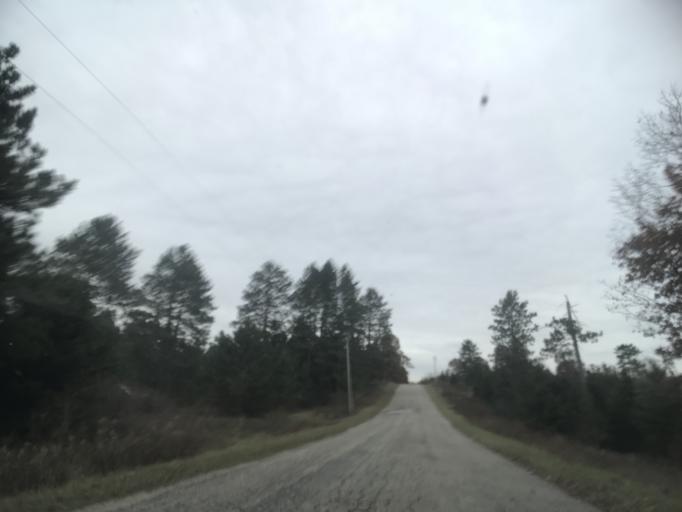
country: US
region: Wisconsin
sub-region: Oconto County
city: Gillett
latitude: 45.3179
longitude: -88.2766
